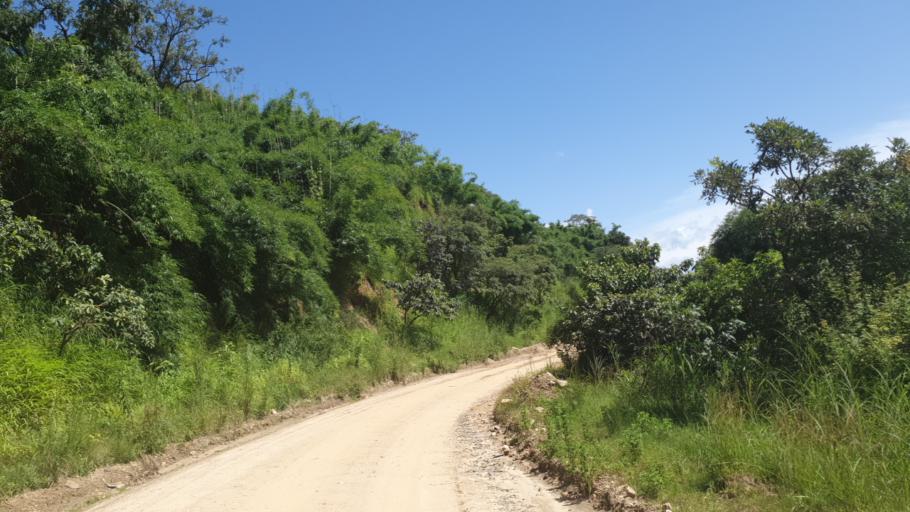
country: ET
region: Oromiya
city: Shambu
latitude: 9.7124
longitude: 36.6281
